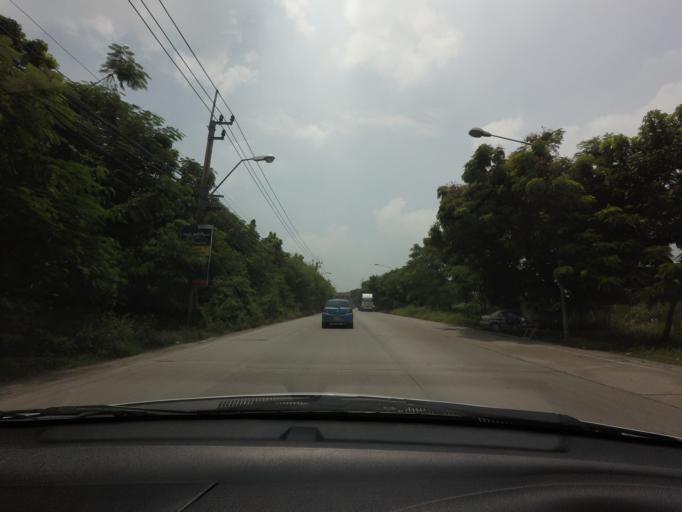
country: TH
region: Bangkok
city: Bang Na
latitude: 13.6570
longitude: 100.6781
